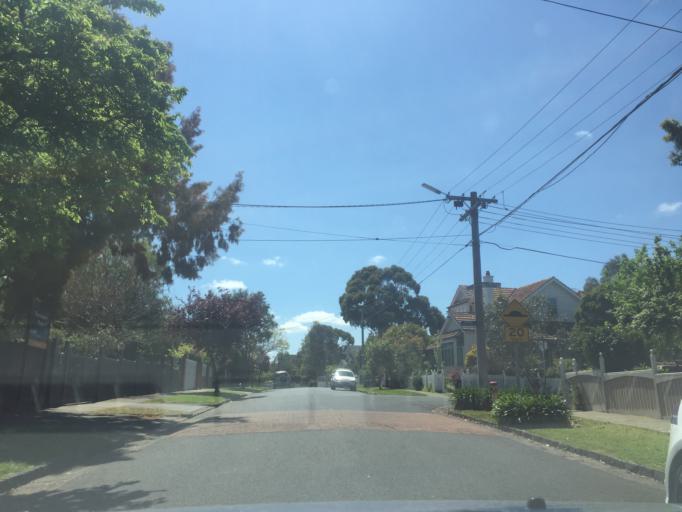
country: AU
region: Victoria
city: Alphington
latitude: -37.7736
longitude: 145.0378
